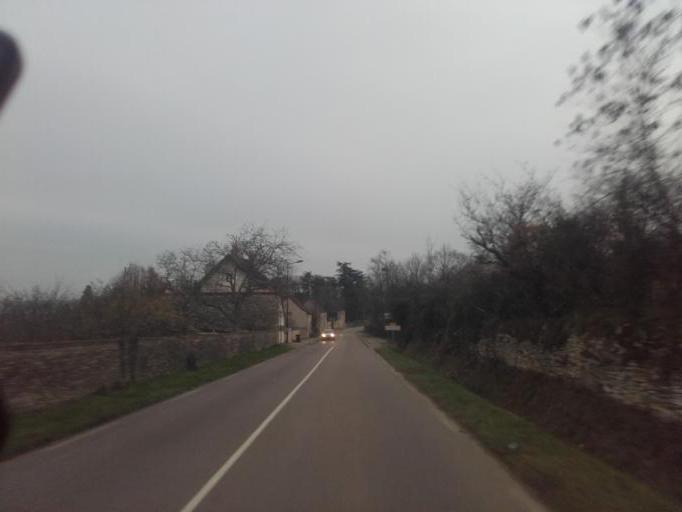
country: FR
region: Bourgogne
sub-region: Departement de Saone-et-Loire
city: Fontaines
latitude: 46.8511
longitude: 4.7544
